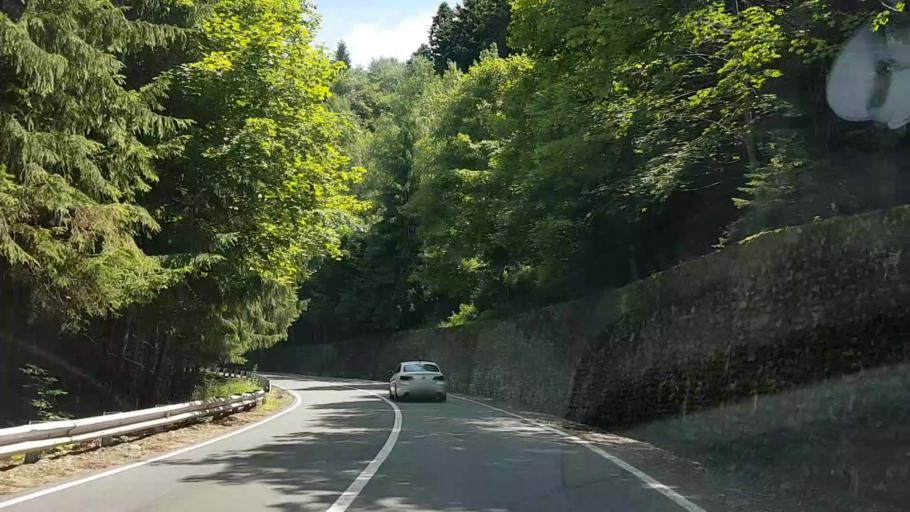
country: RO
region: Sibiu
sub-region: Comuna Cartisoara
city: Cartisoara
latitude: 45.6643
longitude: 24.5880
